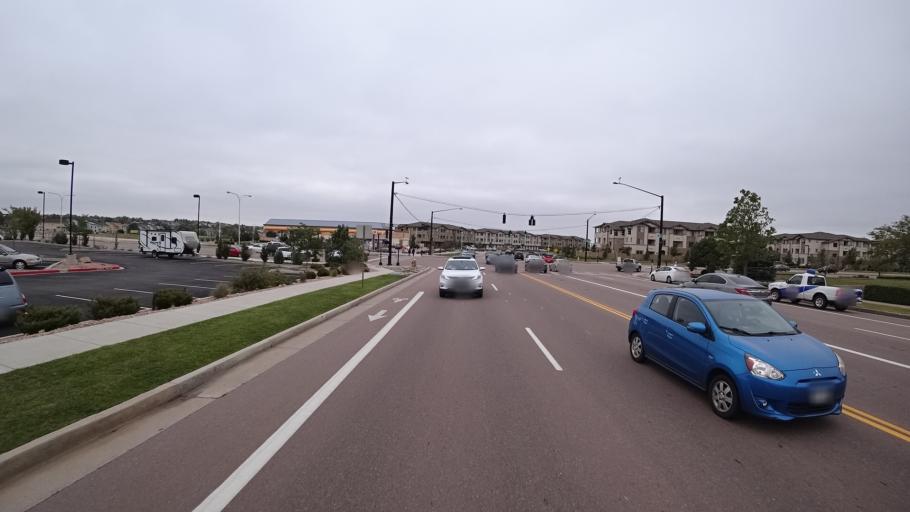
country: US
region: Colorado
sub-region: El Paso County
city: Cimarron Hills
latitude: 38.8864
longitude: -104.7132
